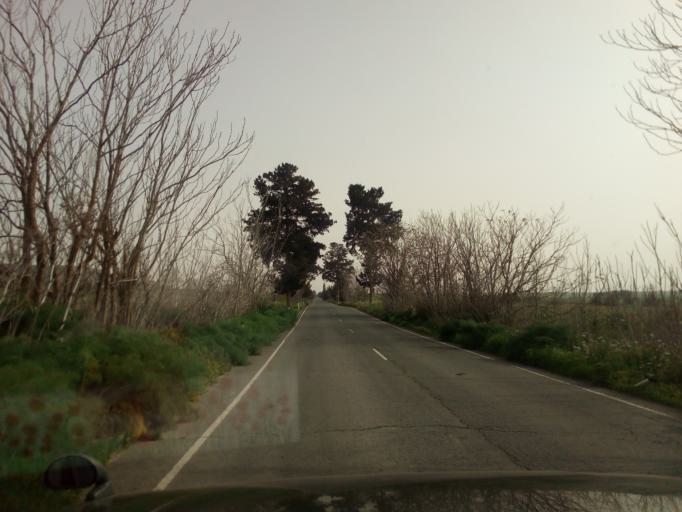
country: CY
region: Lefkosia
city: Lympia
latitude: 35.0257
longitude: 33.4936
